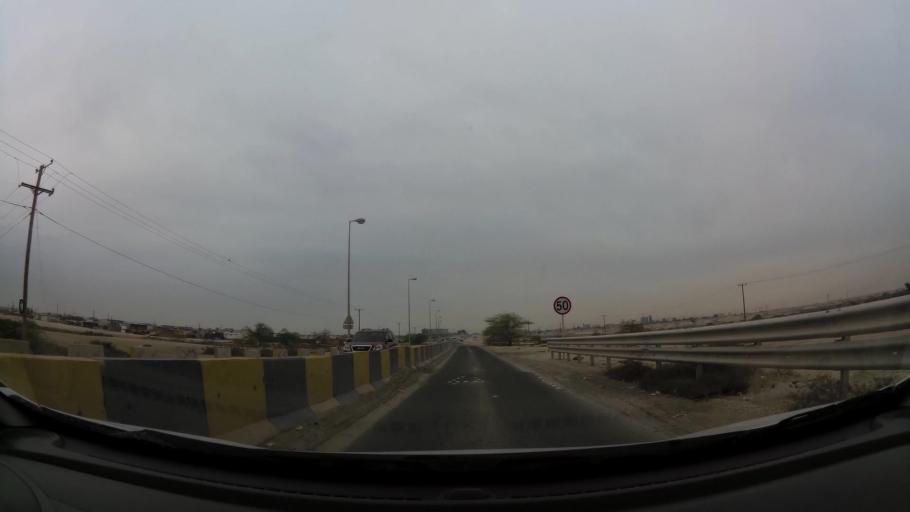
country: BH
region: Northern
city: Ar Rifa'
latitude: 26.0904
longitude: 50.5816
